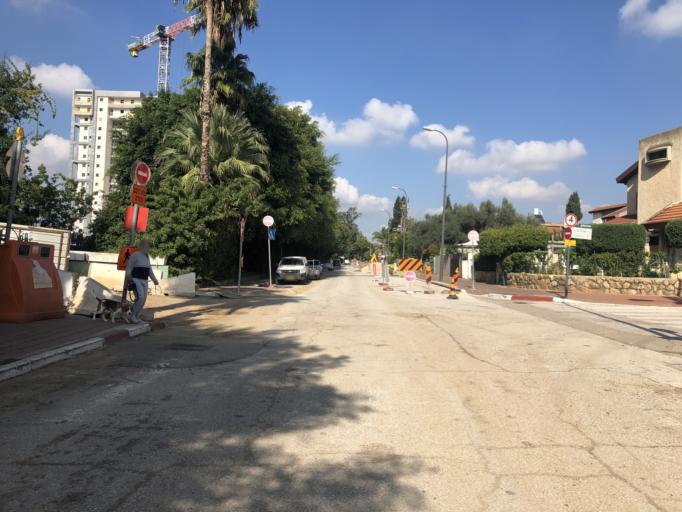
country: IL
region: Central District
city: Yehud
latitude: 32.0264
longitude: 34.8750
